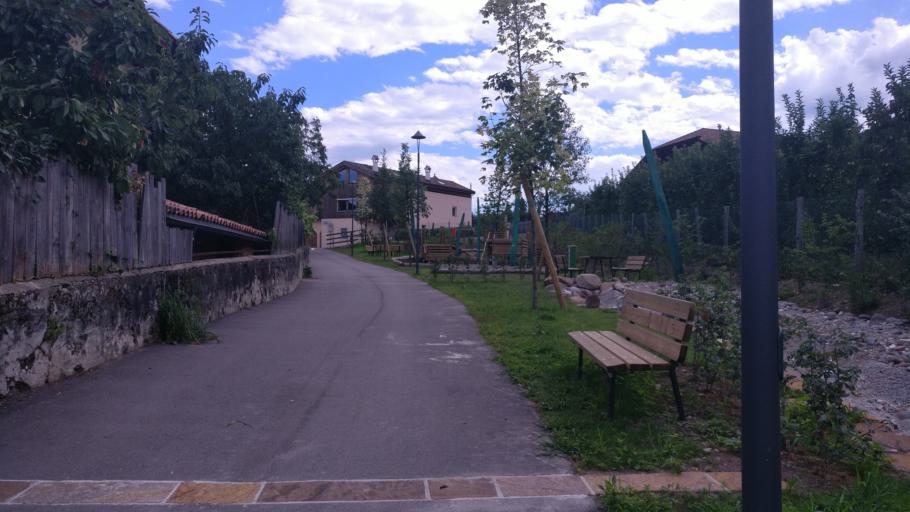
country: IT
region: Trentino-Alto Adige
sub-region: Bolzano
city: San Michele
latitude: 46.4531
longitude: 11.2567
